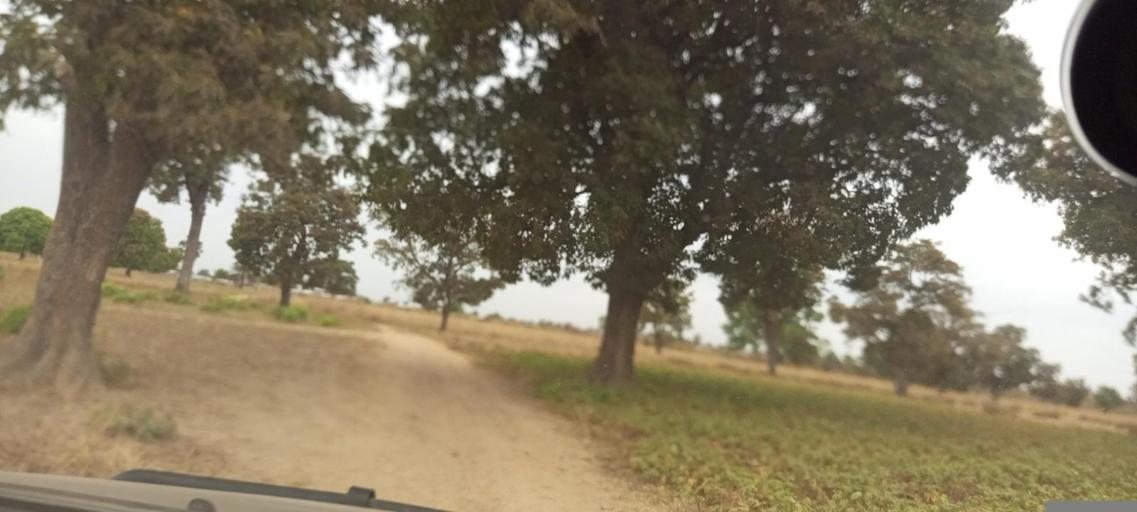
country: ML
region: Koulikoro
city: Kati
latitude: 12.7463
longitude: -8.3565
